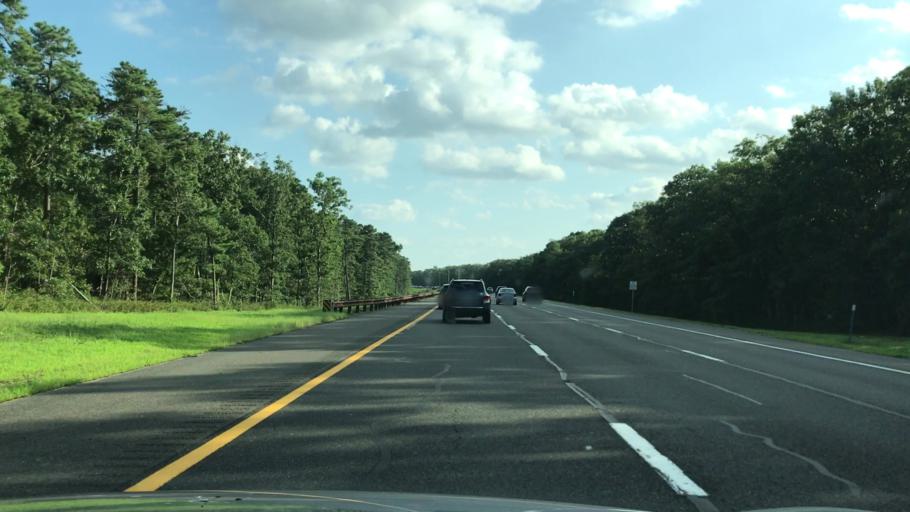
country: US
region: New Jersey
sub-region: Ocean County
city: Barnegat
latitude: 39.7685
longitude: -74.2479
